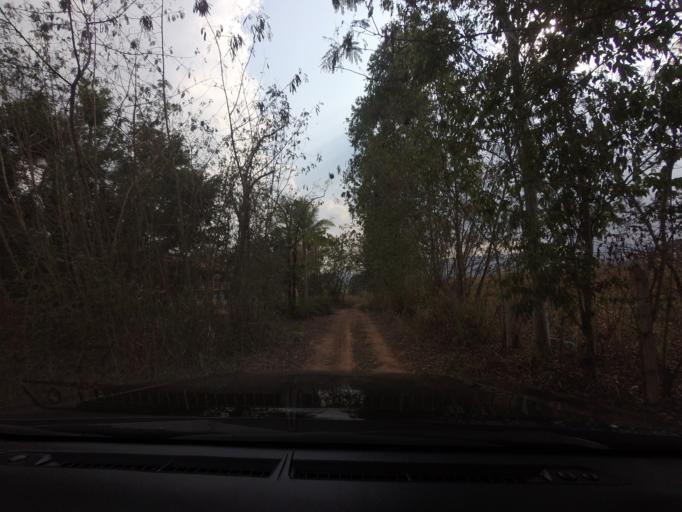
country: TH
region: Nakhon Ratchasima
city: Wang Nam Khiao
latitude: 14.4752
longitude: 101.6553
